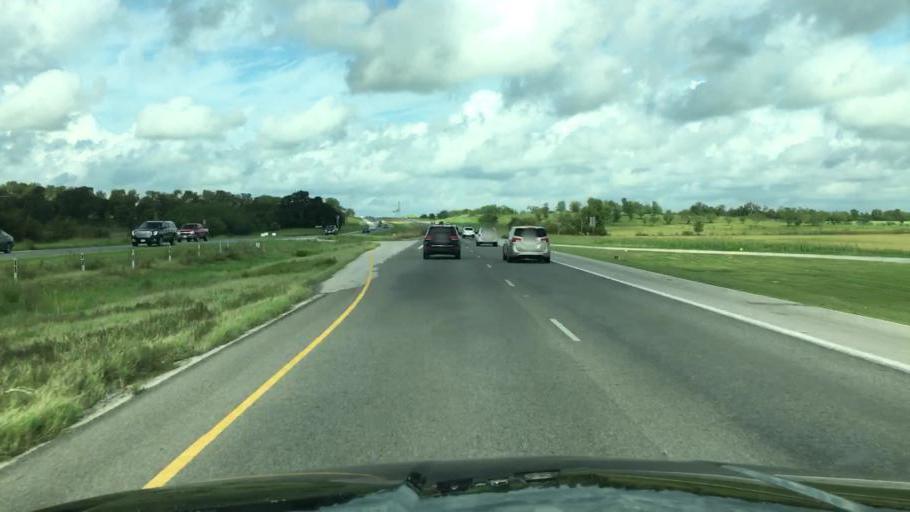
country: US
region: Texas
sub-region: Travis County
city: Garfield
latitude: 30.1671
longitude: -97.5123
